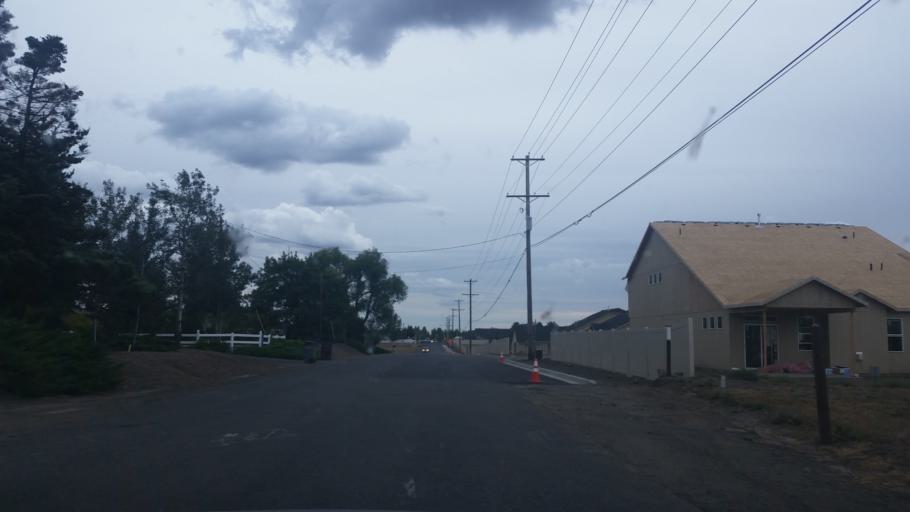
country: US
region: Washington
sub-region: Spokane County
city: Cheney
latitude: 47.5112
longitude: -117.5756
